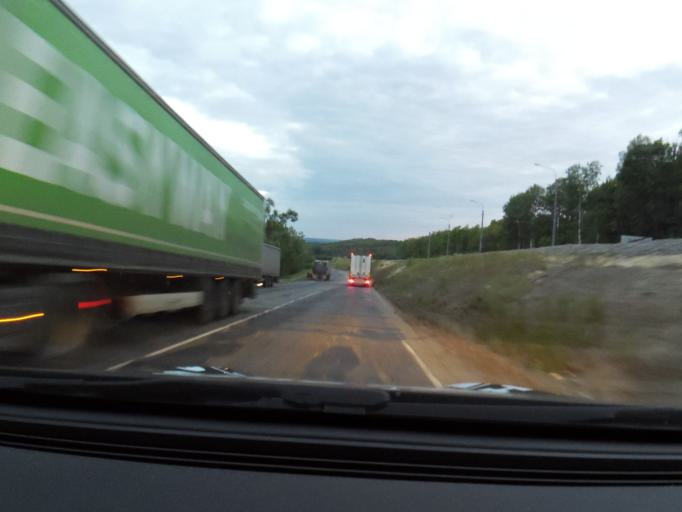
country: RU
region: Chuvashia
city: Yadrin
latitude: 56.0389
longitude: 46.2686
